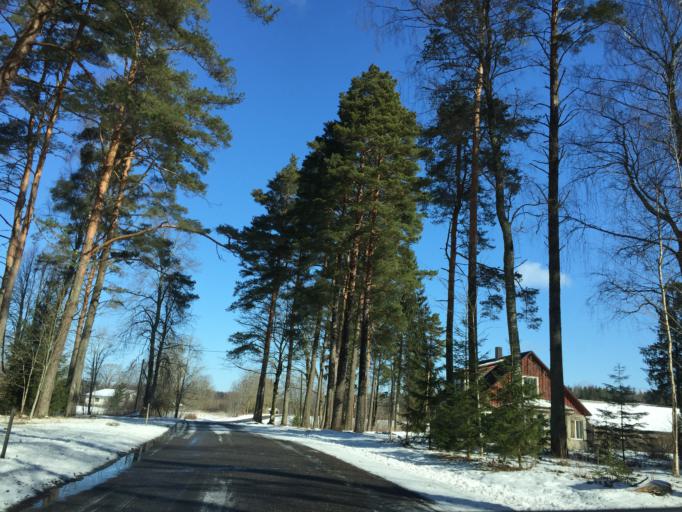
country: LV
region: Aloja
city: Staicele
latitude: 58.0000
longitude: 24.5878
